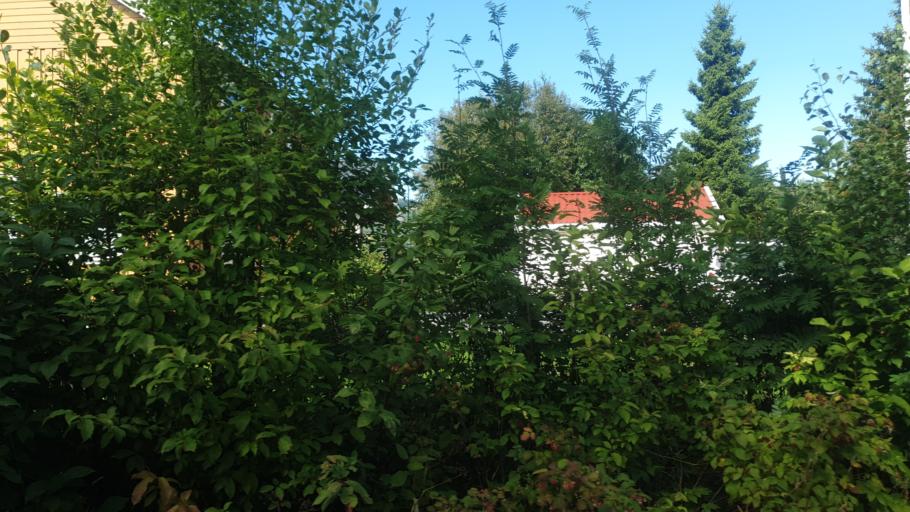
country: NO
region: Sor-Trondelag
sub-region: Orkdal
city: Orkanger
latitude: 63.2780
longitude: 9.8267
